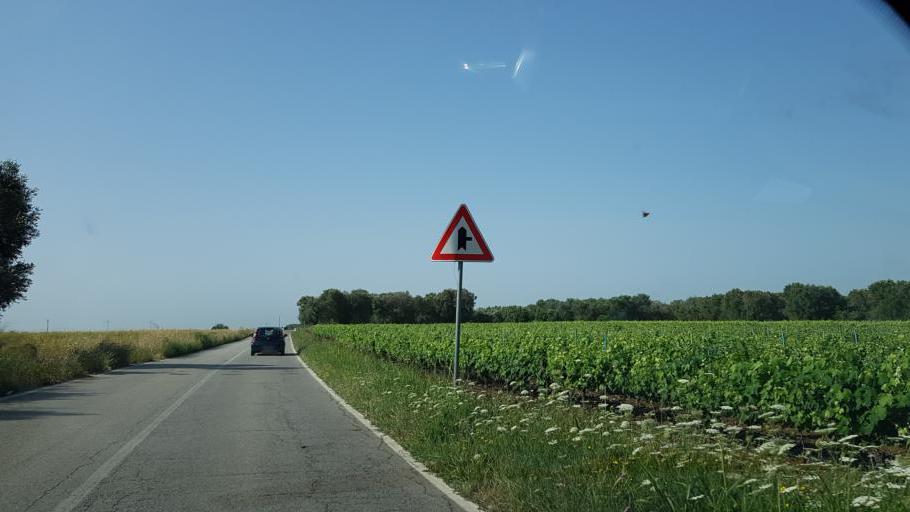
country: IT
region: Apulia
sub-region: Provincia di Brindisi
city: Mesagne
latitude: 40.5114
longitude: 17.8270
